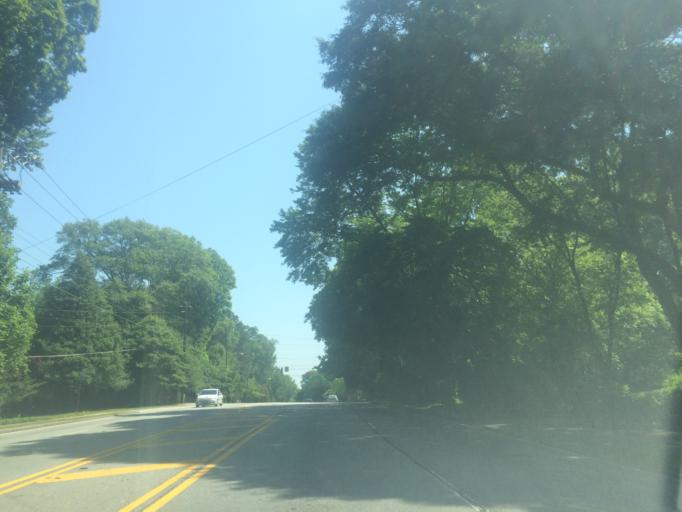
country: US
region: Georgia
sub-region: DeKalb County
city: North Decatur
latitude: 33.7872
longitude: -84.3005
